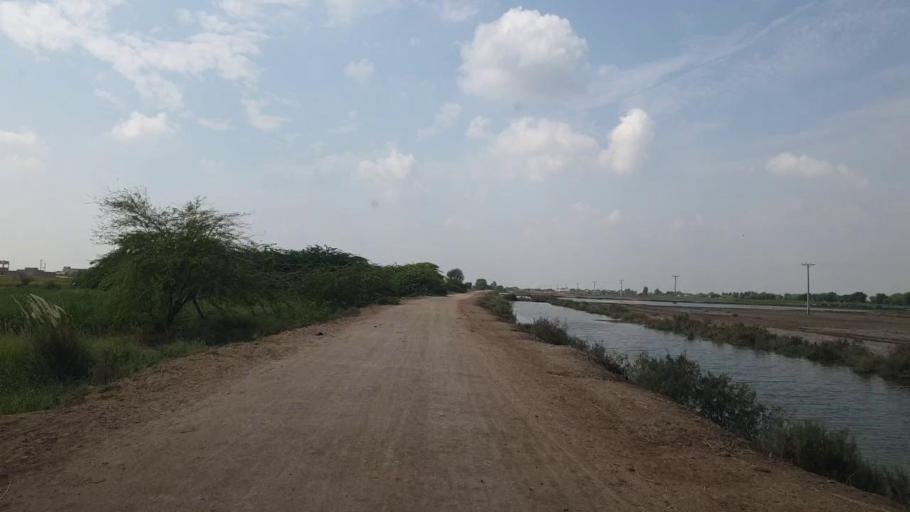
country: PK
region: Sindh
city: Badin
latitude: 24.5066
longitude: 68.6544
